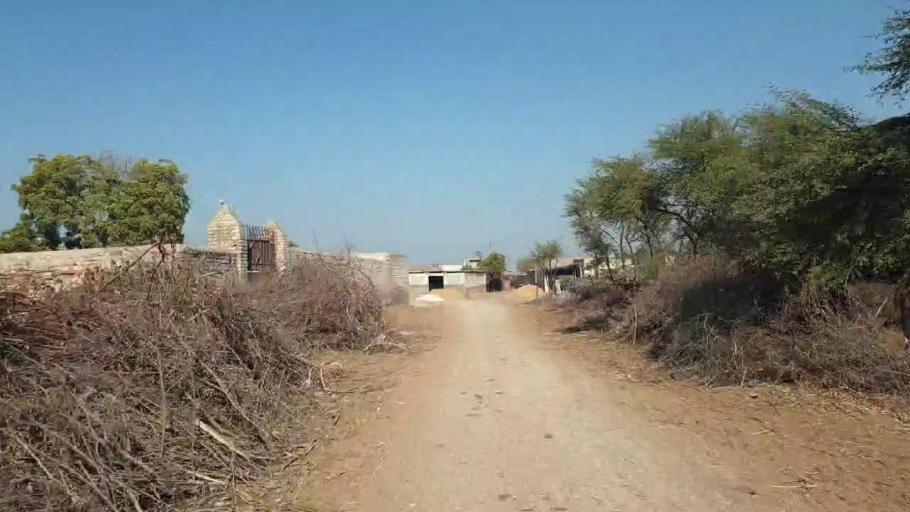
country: PK
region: Sindh
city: Shahdadpur
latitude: 25.9518
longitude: 68.5112
